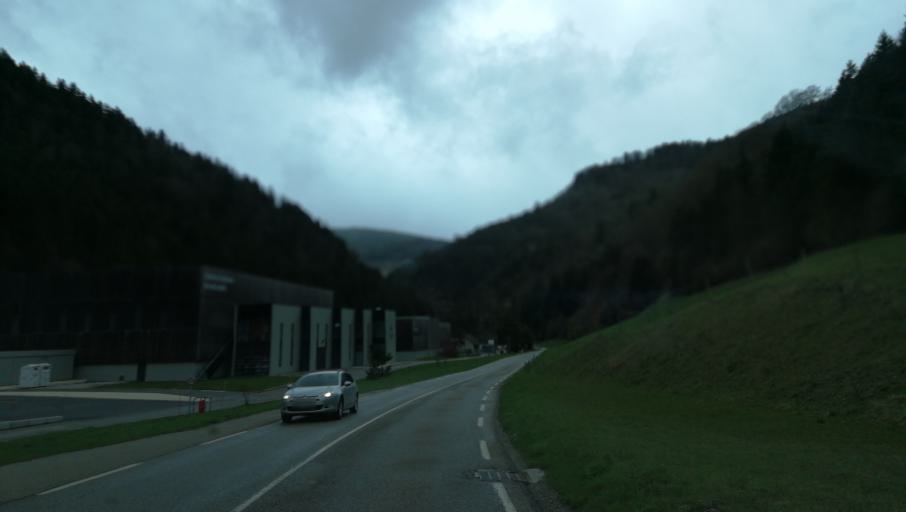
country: FR
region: Rhone-Alpes
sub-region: Departement de l'Isere
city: Villard-de-Lans
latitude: 45.0795
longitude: 5.5344
